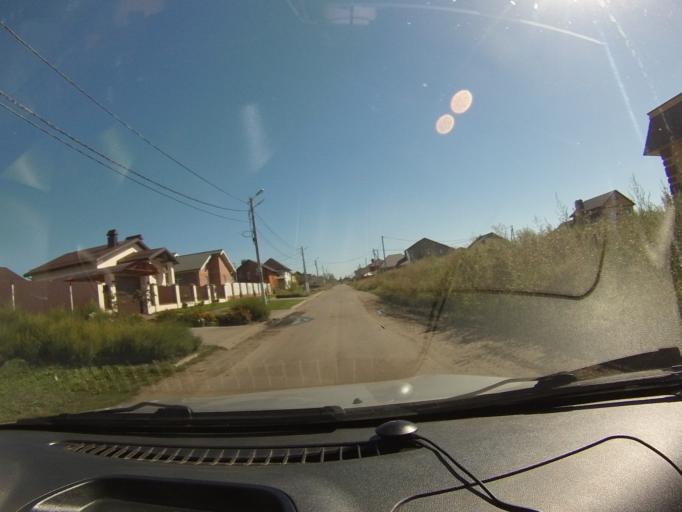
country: RU
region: Tambov
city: Komsomolets
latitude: 52.7731
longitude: 41.3581
